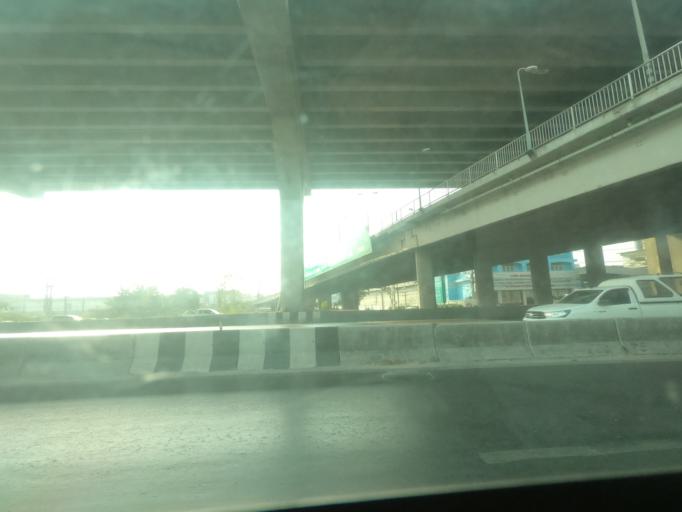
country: TH
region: Bangkok
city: Sai Mai
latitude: 13.9607
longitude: 100.6406
